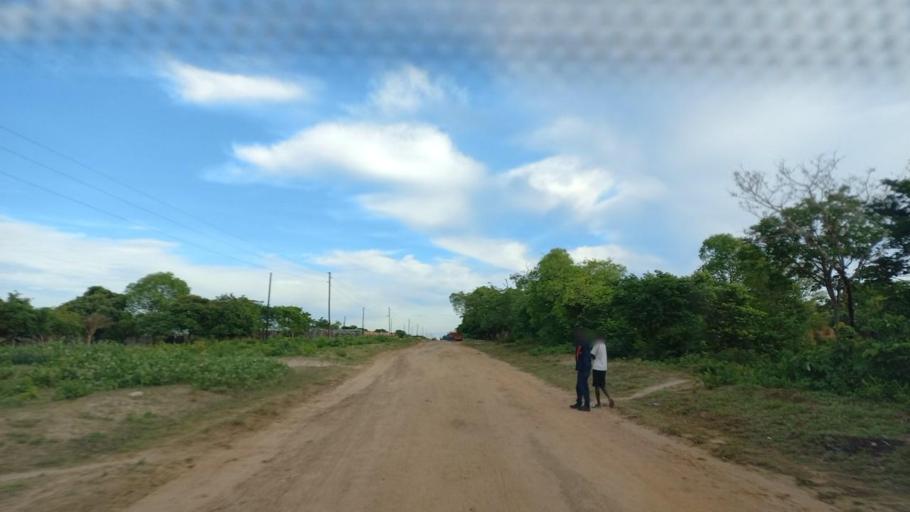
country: ZM
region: North-Western
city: Kabompo
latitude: -13.4211
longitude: 24.3226
